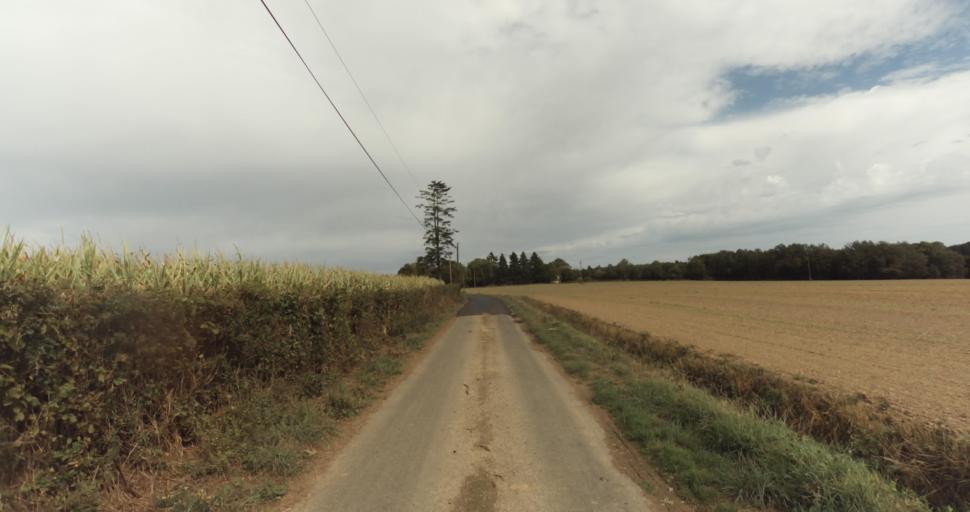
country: FR
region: Lower Normandy
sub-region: Departement du Calvados
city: Orbec
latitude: 48.9410
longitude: 0.3625
